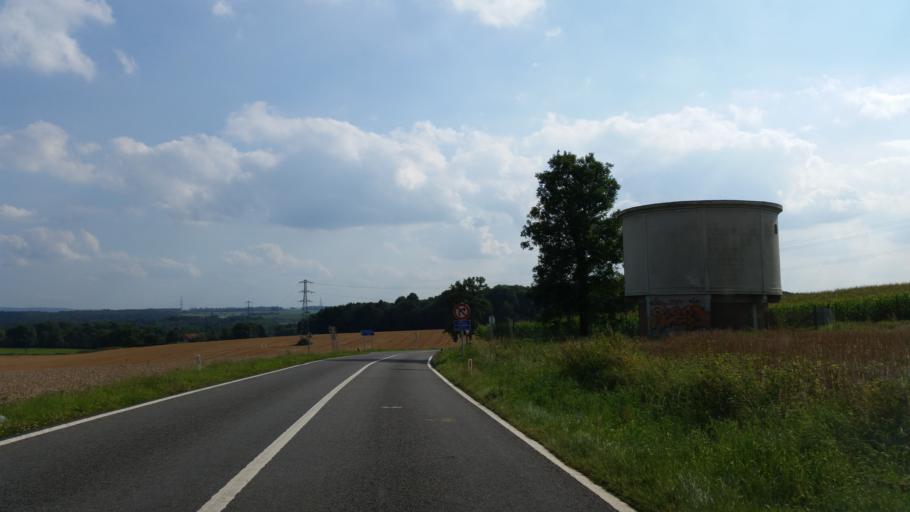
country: BE
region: Wallonia
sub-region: Province de Liege
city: Anthisnes
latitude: 50.4766
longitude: 5.4904
